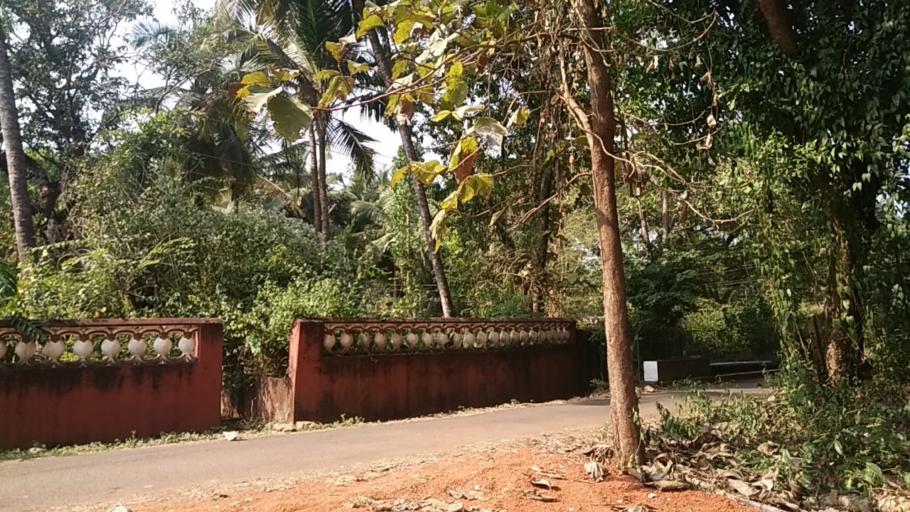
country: IN
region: Goa
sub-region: South Goa
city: Chinchinim
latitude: 15.2104
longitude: 73.9806
